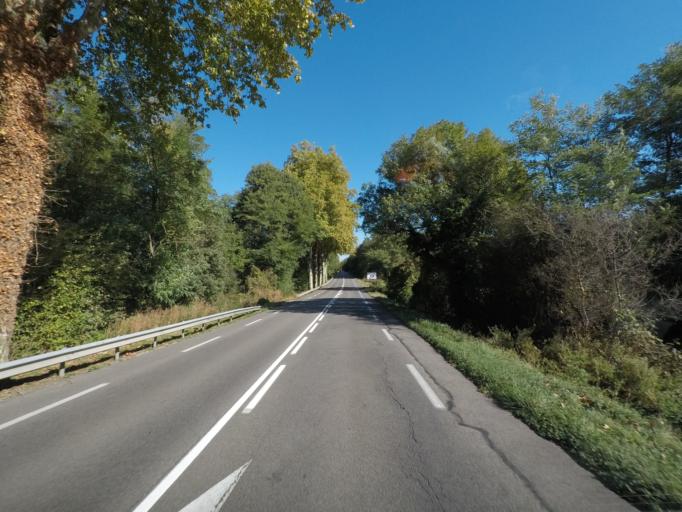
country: FR
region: Rhone-Alpes
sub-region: Departement de l'Ain
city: Servas
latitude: 46.1434
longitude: 5.1734
